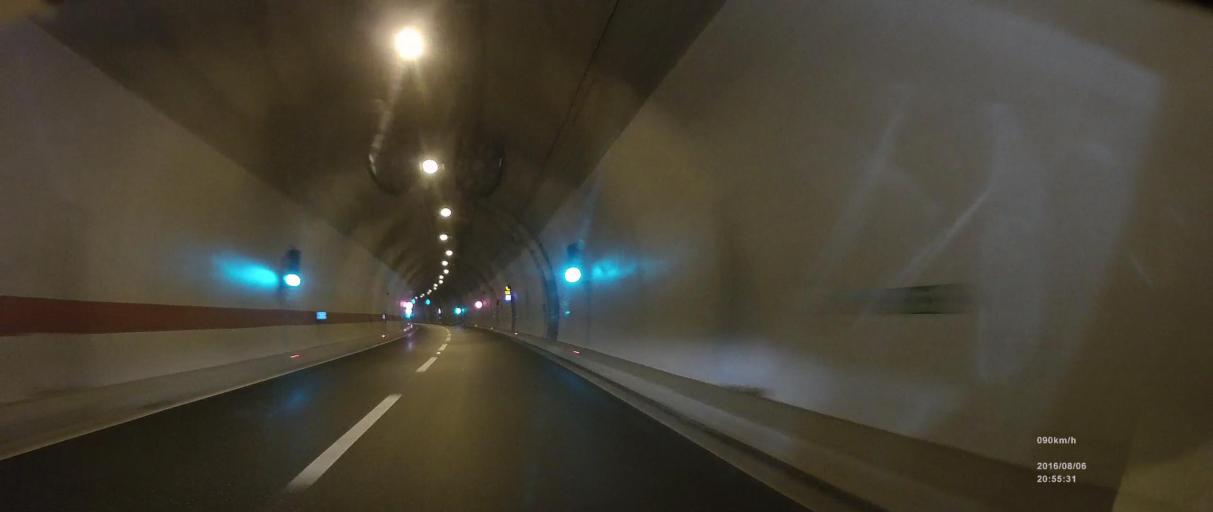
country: BA
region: Federation of Bosnia and Herzegovina
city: Vitina
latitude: 43.1623
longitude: 17.4705
